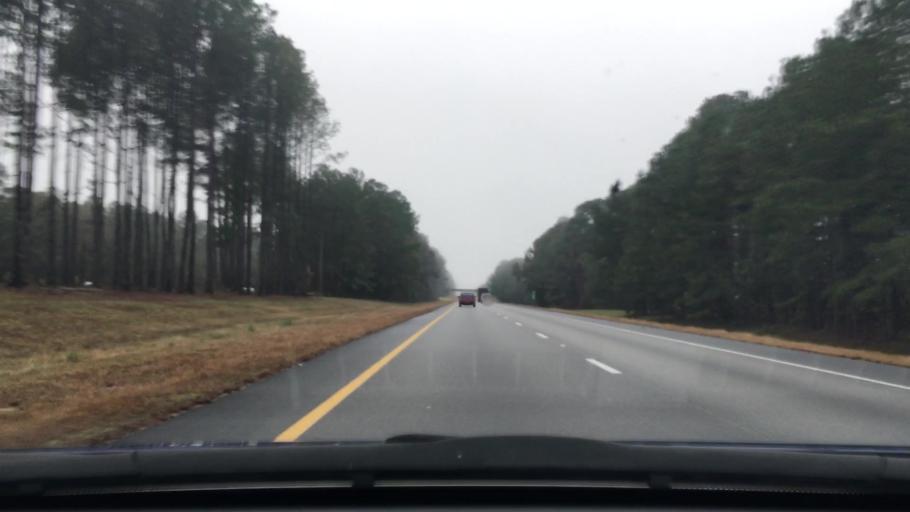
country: US
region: South Carolina
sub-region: Lee County
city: Bishopville
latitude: 34.2030
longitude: -80.3653
